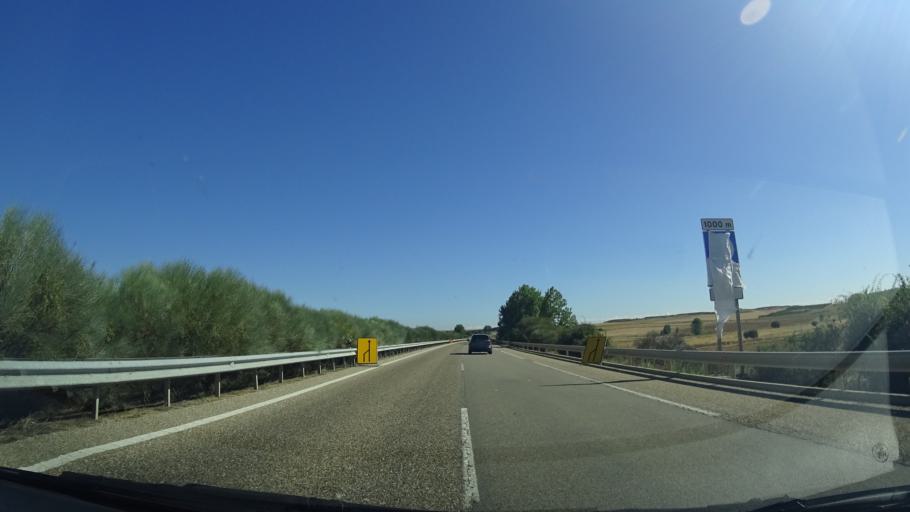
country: ES
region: Castille and Leon
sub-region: Provincia de Zamora
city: Matilla de Arzon
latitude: 42.1137
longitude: -5.6583
